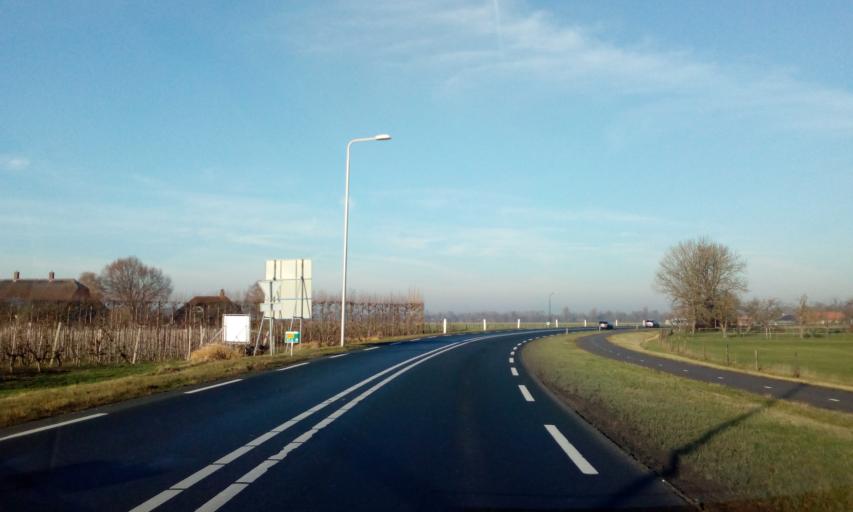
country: NL
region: Utrecht
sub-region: Gemeente Montfoort
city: Montfoort
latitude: 52.0474
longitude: 4.9288
